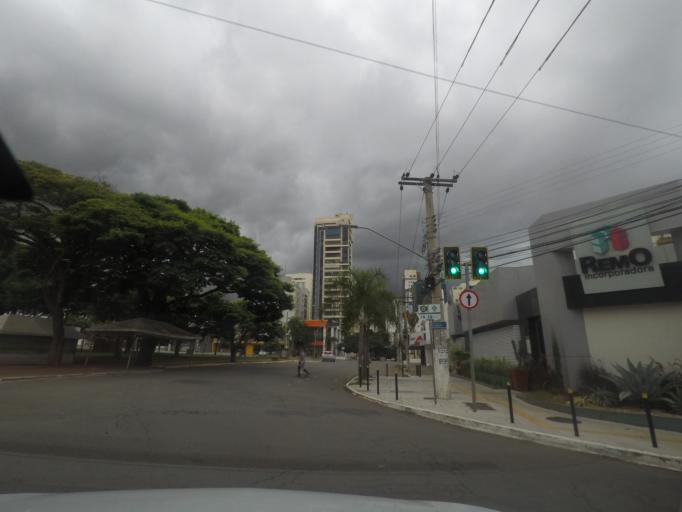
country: BR
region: Goias
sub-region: Goiania
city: Goiania
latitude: -16.6844
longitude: -49.2659
